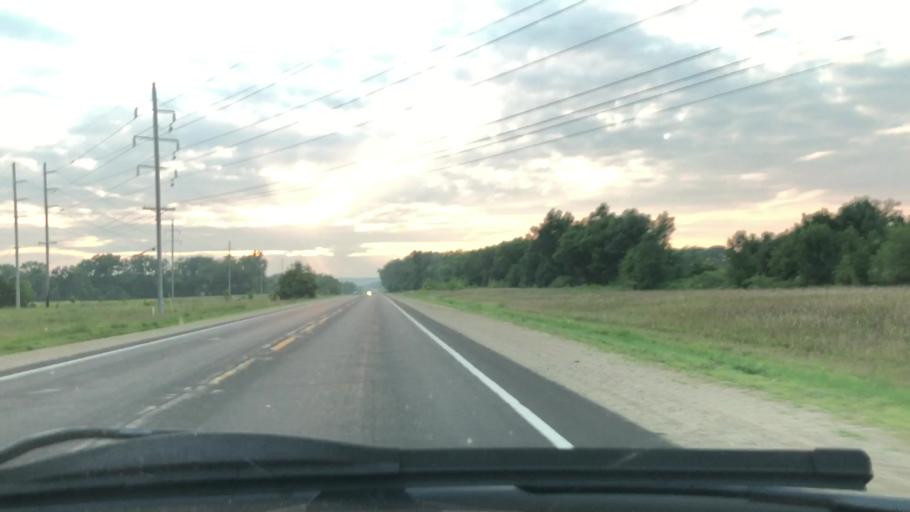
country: US
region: Wisconsin
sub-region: Sauk County
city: Spring Green
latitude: 43.1984
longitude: -90.2381
